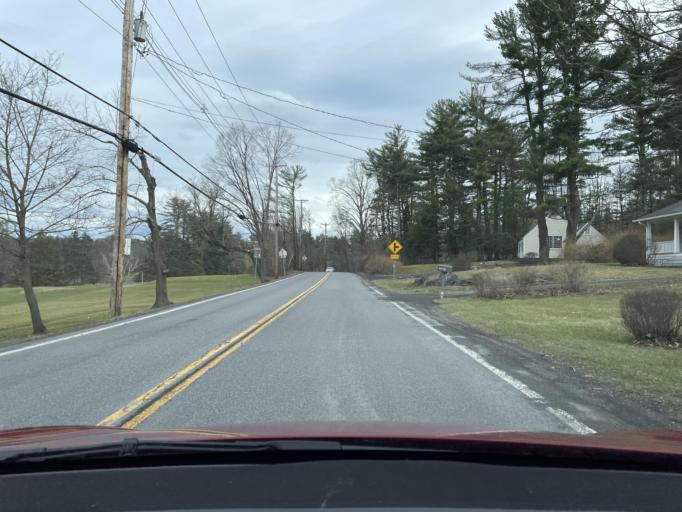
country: US
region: New York
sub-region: Ulster County
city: Woodstock
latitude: 42.0345
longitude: -74.1100
